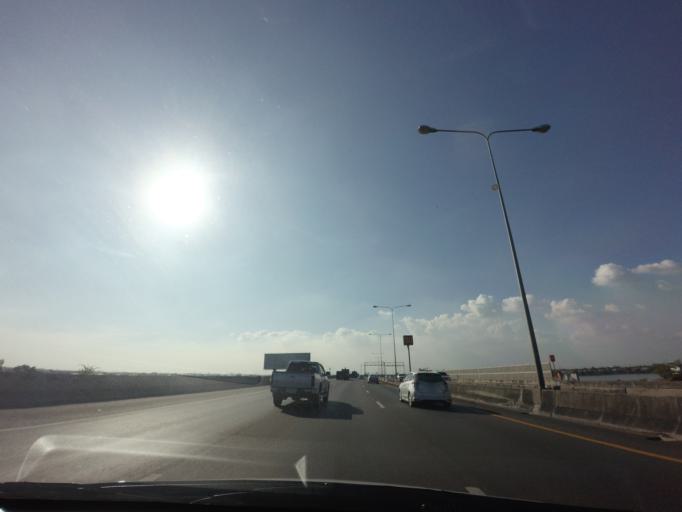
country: TH
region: Samut Prakan
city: Samut Prakan
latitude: 13.6002
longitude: 100.6438
